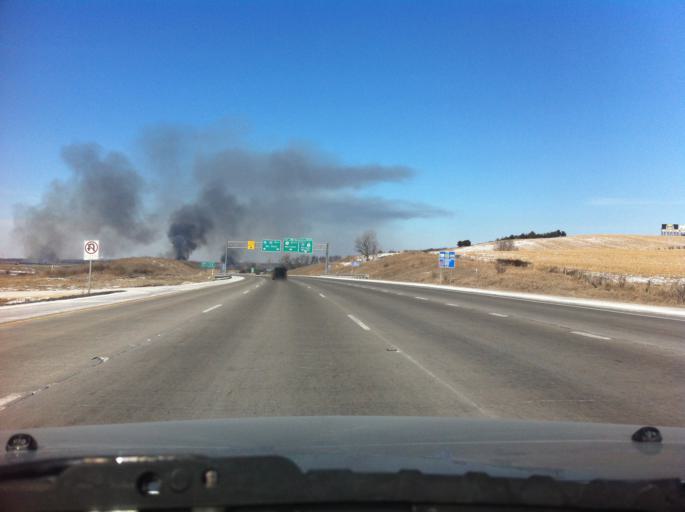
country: US
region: Wisconsin
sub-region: Columbia County
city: Portage
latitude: 43.4480
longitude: -89.4939
